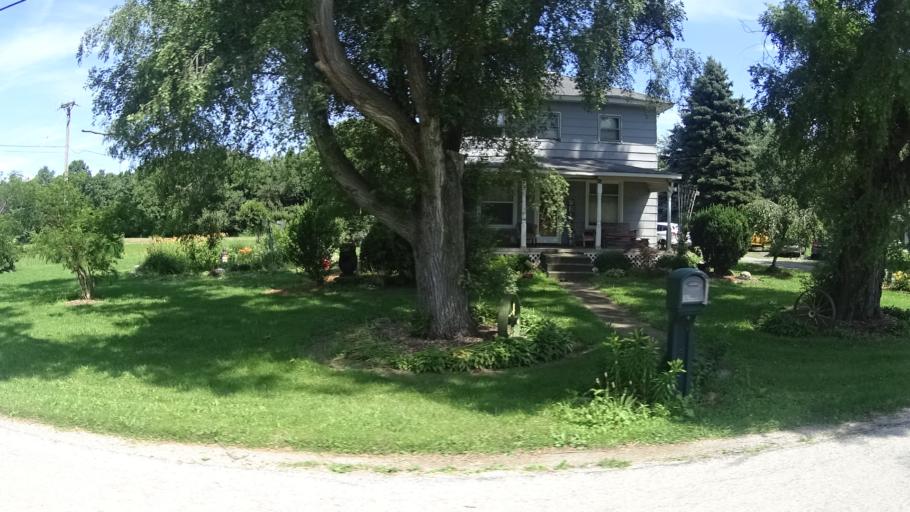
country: US
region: Ohio
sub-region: Erie County
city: Huron
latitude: 41.3538
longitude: -82.4527
